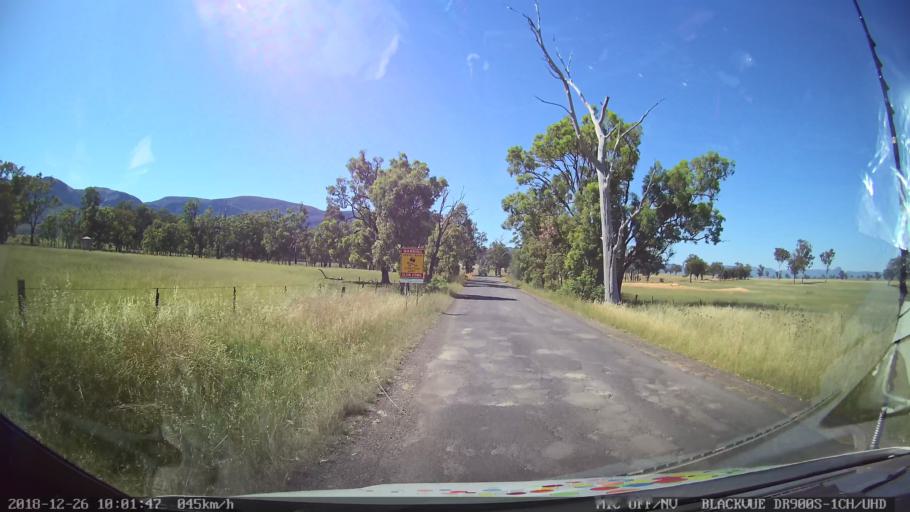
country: AU
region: New South Wales
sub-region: Mid-Western Regional
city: Kandos
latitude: -33.0495
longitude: 150.2228
